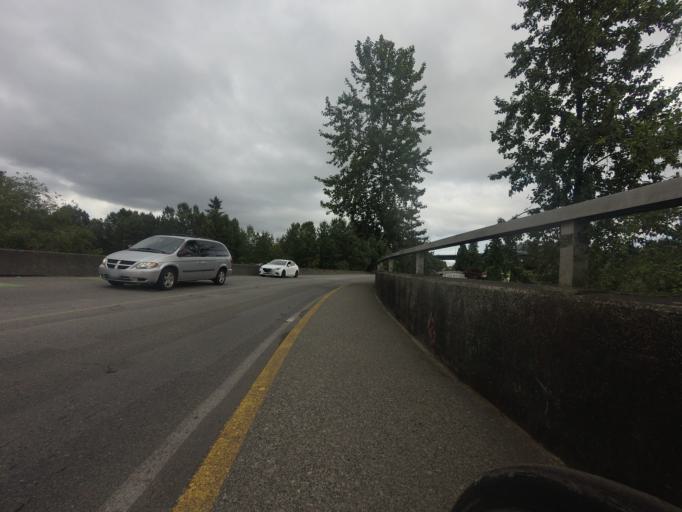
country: CA
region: British Columbia
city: West End
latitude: 49.3247
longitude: -123.1338
